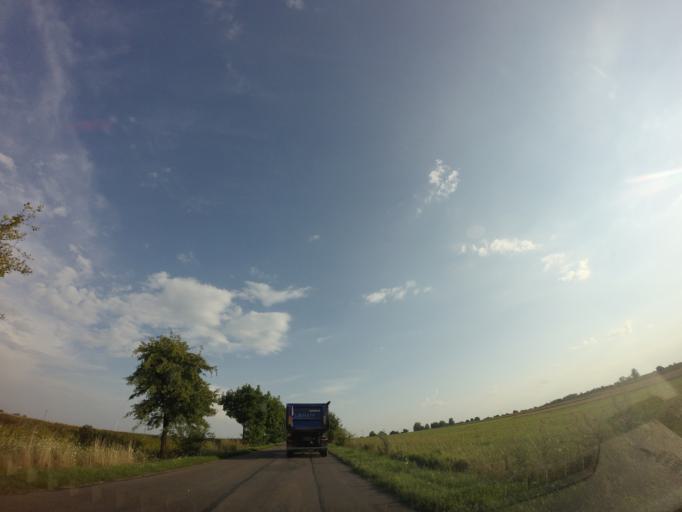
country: PL
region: Lublin Voivodeship
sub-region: Powiat lubartowski
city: Michow
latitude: 51.4997
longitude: 22.3065
